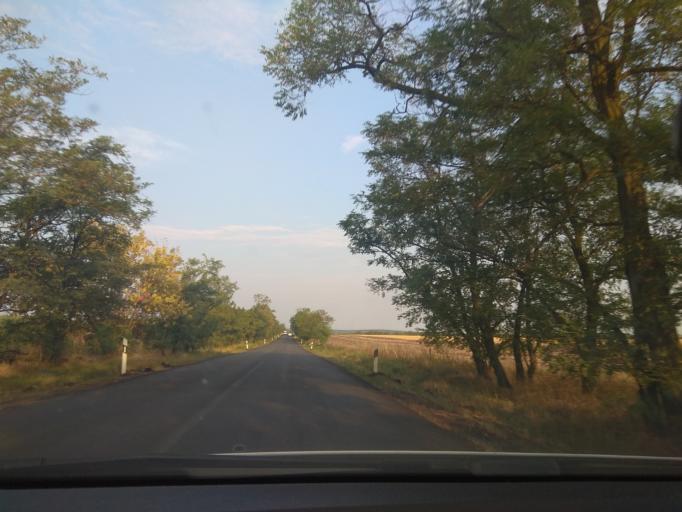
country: HU
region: Heves
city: Szihalom
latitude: 47.8169
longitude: 20.5133
